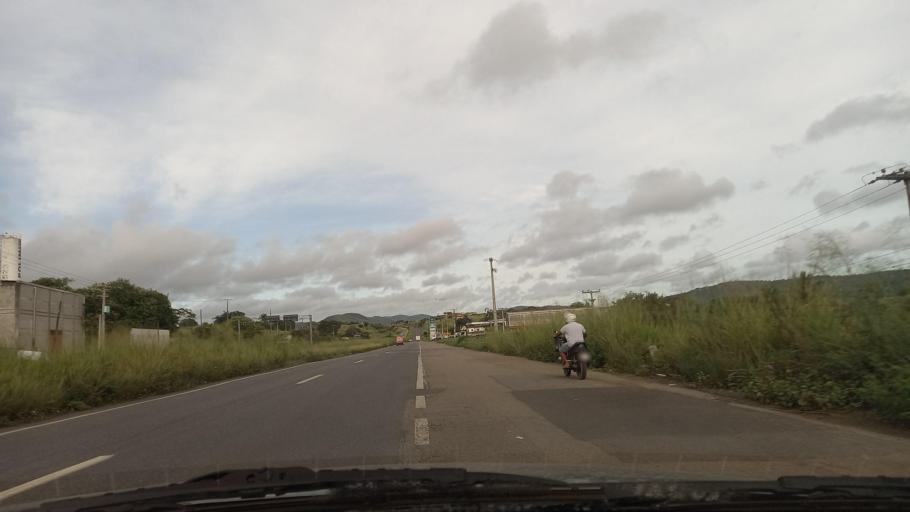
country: BR
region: Pernambuco
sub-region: Pombos
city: Pombos
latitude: -8.1287
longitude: -35.3559
